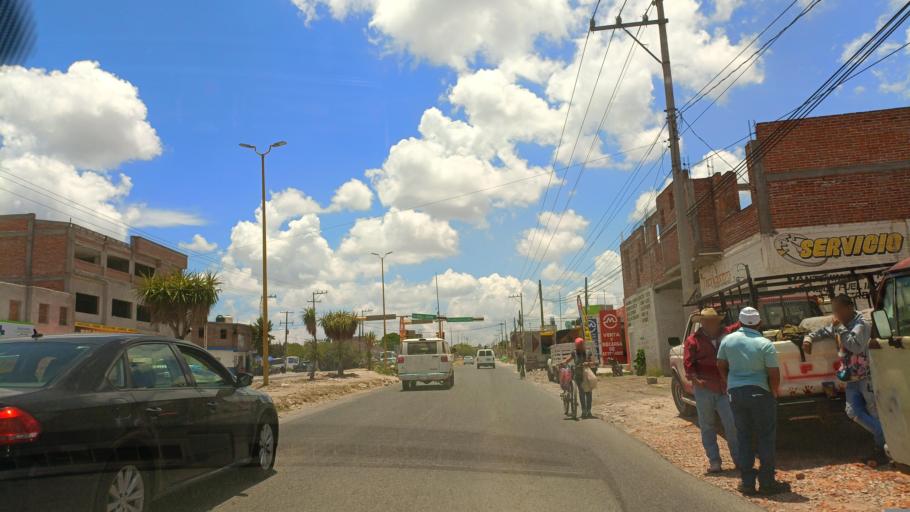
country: MX
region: Guanajuato
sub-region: San Luis de la Paz
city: San Ignacio
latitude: 21.2875
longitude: -100.5315
